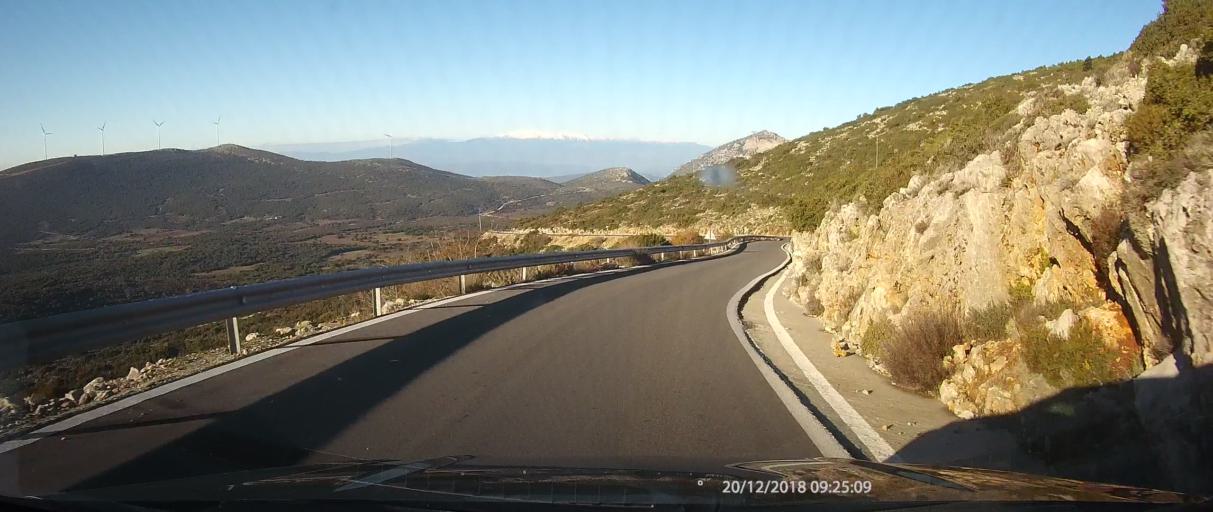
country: GR
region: Peloponnese
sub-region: Nomos Lakonias
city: Molaoi
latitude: 36.9596
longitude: 22.8884
